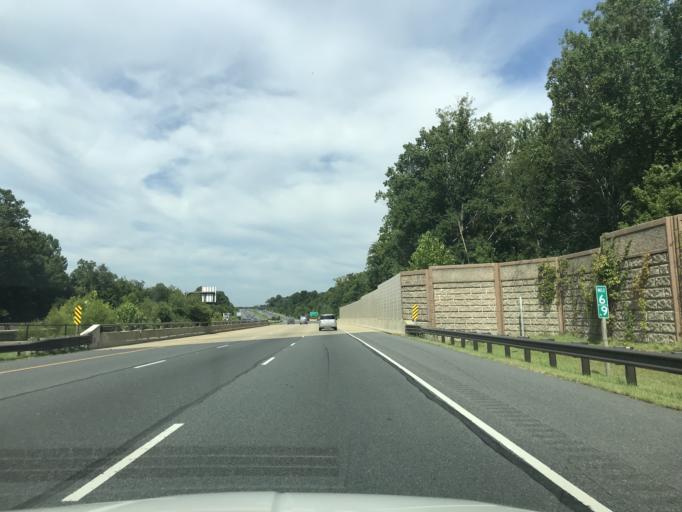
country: US
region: Maryland
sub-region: Montgomery County
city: Rossmoor
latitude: 39.1258
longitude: -77.0968
